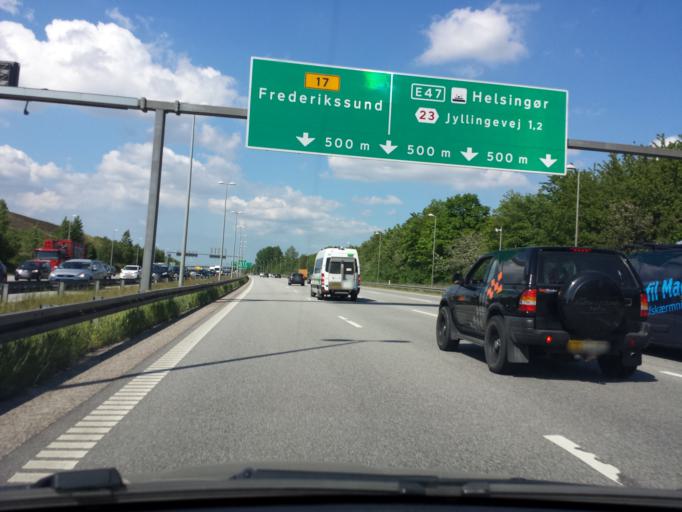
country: DK
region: Capital Region
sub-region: Glostrup Kommune
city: Glostrup
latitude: 55.6785
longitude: 12.4264
